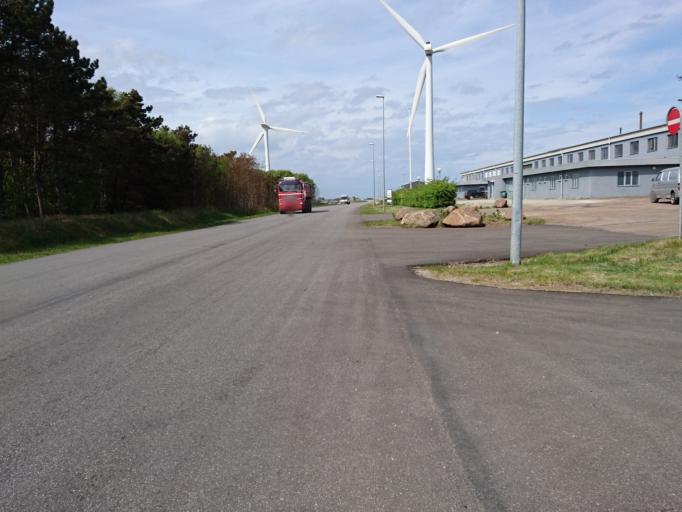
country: DK
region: North Denmark
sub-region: Frederikshavn Kommune
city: Skagen
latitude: 57.7345
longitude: 10.5679
